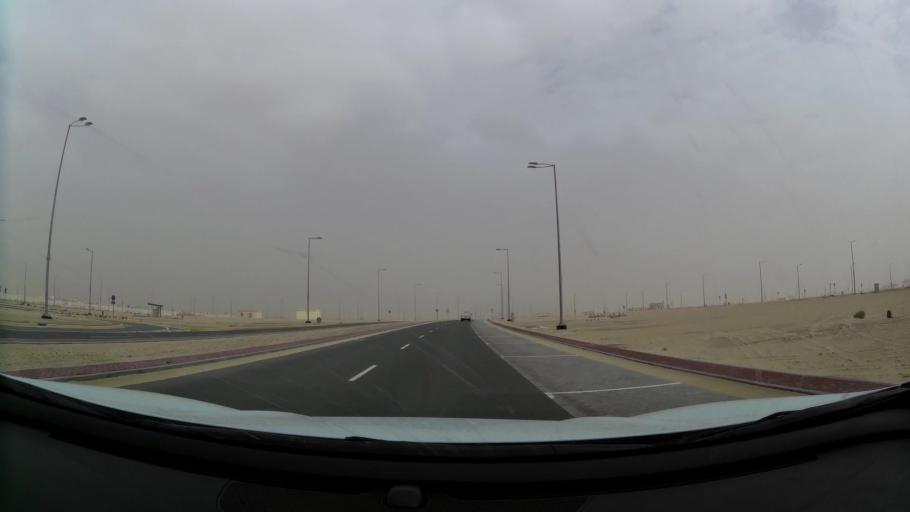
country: AE
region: Abu Dhabi
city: Abu Dhabi
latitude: 24.3670
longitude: 54.7431
